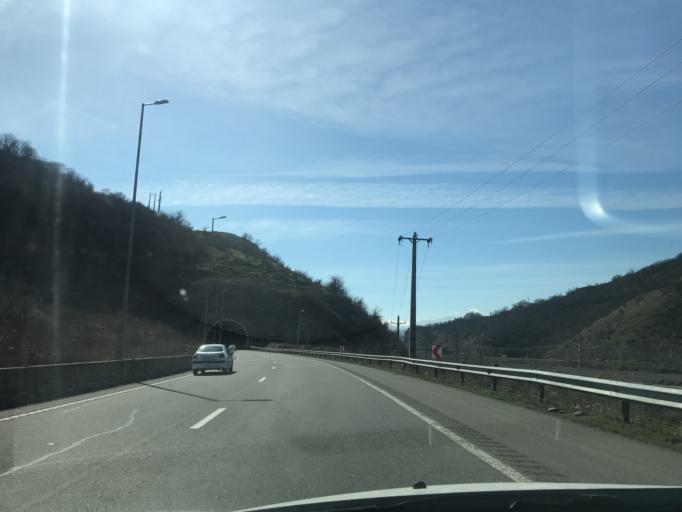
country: IR
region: Gilan
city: Pa'in-e Bazar-e Rudbar
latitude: 36.9531
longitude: 49.5501
